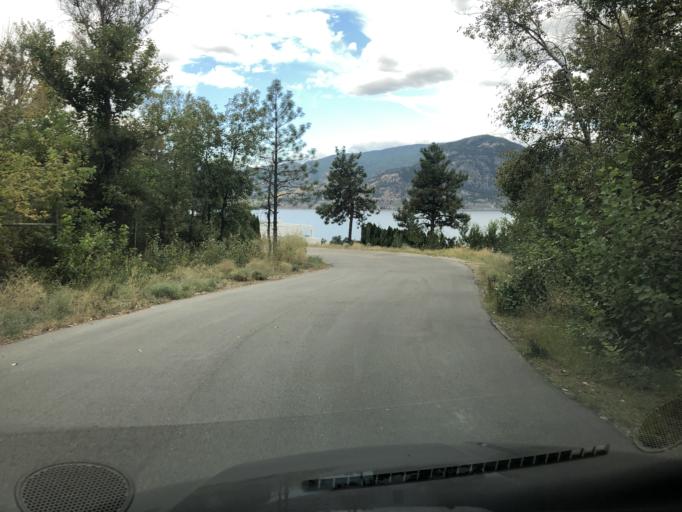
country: CA
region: British Columbia
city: Penticton
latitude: 49.5468
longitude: -119.5681
